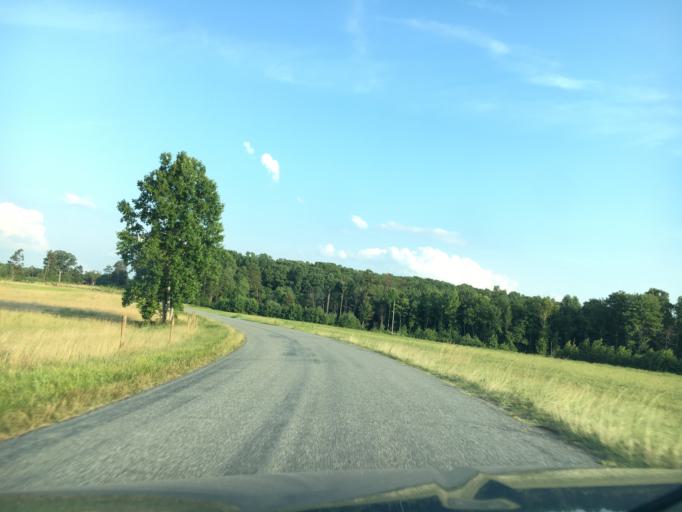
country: US
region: Virginia
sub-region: Halifax County
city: Mountain Road
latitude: 36.8420
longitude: -79.1547
